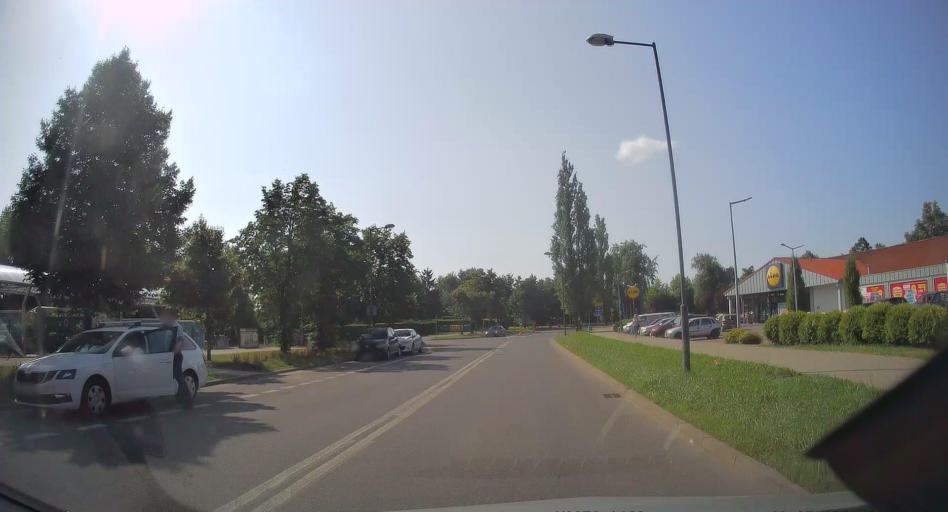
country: PL
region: Silesian Voivodeship
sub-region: Swietochlowice
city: Swietochlowice
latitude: 50.3079
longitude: 18.9126
